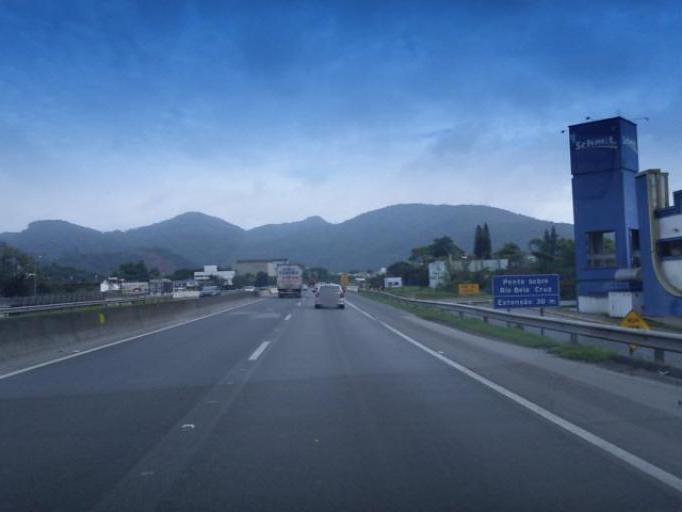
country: BR
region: Santa Catarina
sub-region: Itapema
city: Itapema
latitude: -27.0948
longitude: -48.6181
